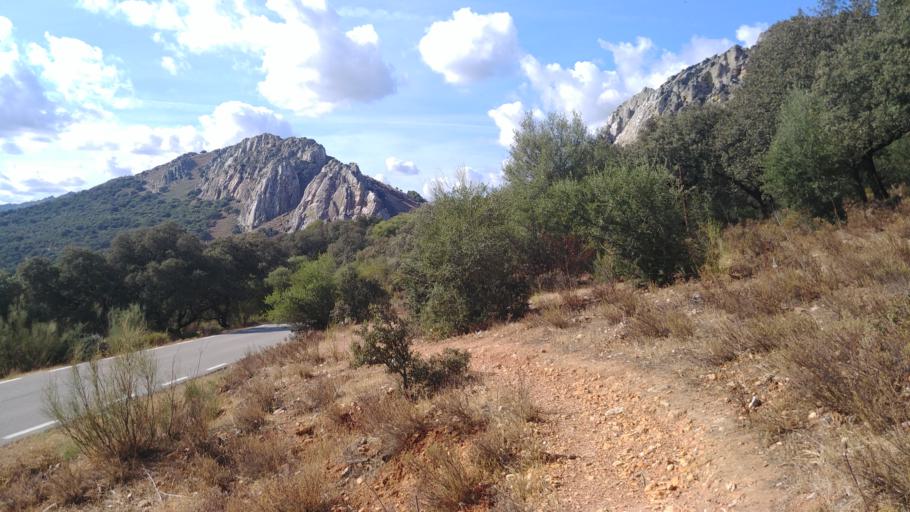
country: ES
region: Extremadura
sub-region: Provincia de Caceres
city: Torrejon el Rubio
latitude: 39.8237
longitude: -6.0519
